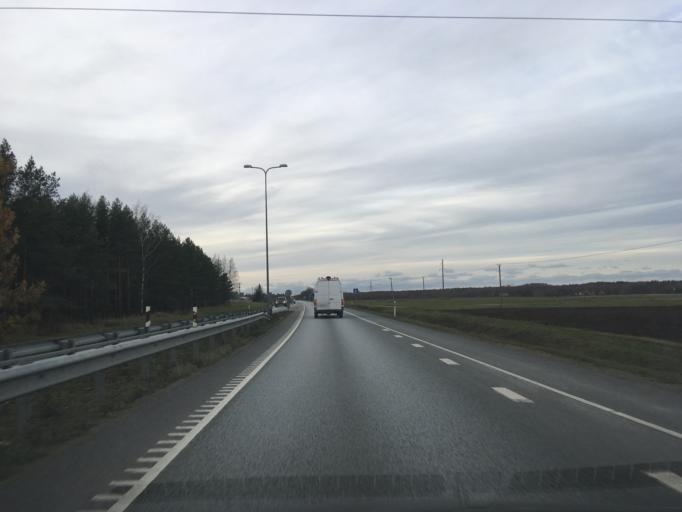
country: EE
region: Ida-Virumaa
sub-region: Kohtla-Jaerve linn
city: Kohtla-Jarve
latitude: 59.4077
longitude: 27.3190
